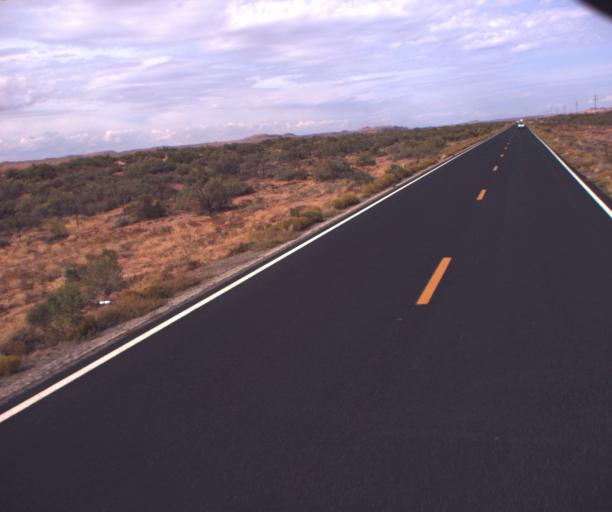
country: US
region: Arizona
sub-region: Apache County
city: Many Farms
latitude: 36.6316
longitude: -109.5854
